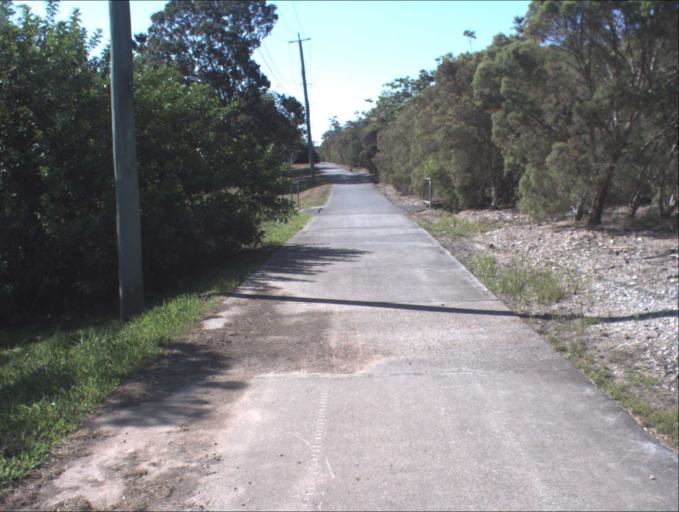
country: AU
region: Queensland
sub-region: Logan
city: Beenleigh
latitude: -27.6920
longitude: 153.1923
